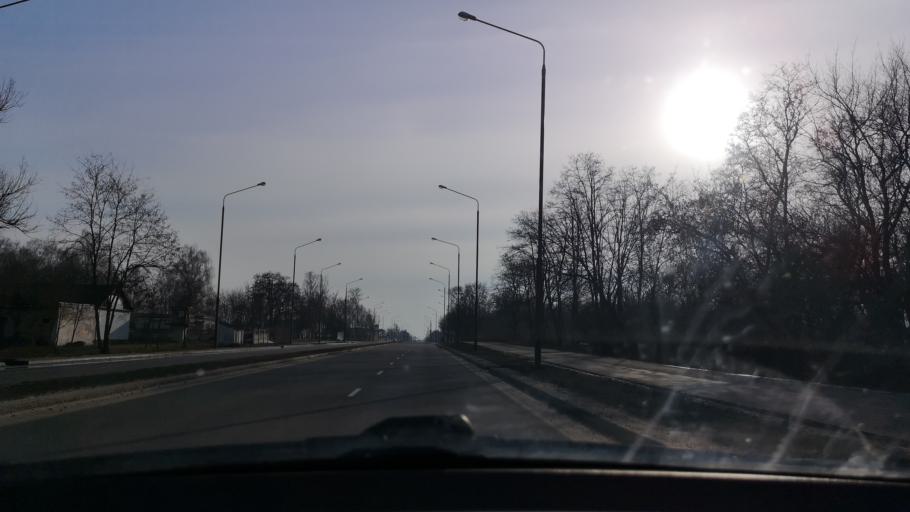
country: BY
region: Brest
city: Brest
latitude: 52.1260
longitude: 23.6725
